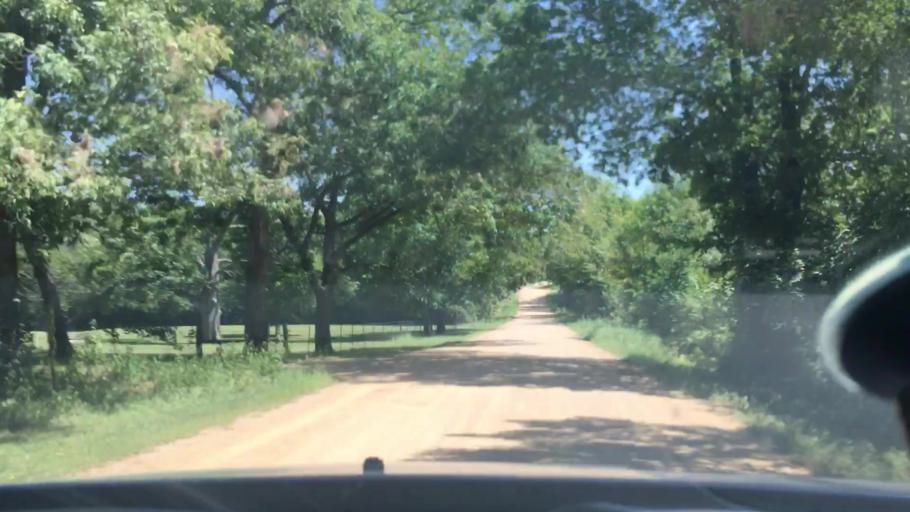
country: US
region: Oklahoma
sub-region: Coal County
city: Coalgate
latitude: 34.3681
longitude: -96.4272
